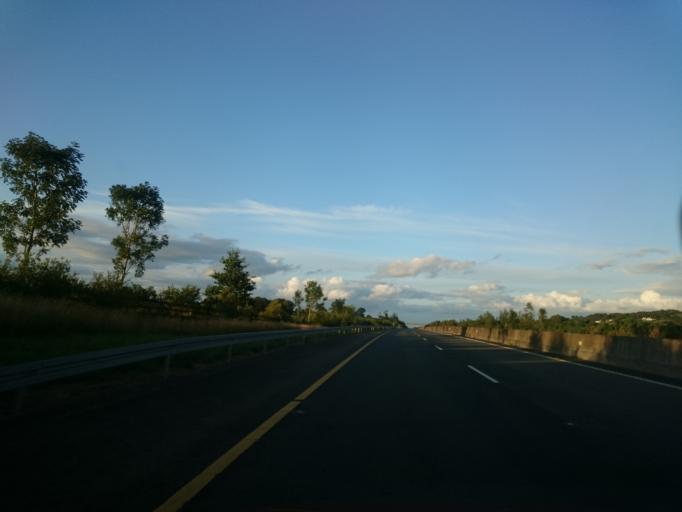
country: IE
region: Leinster
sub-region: Loch Garman
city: Gorey
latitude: 52.6456
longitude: -6.3305
